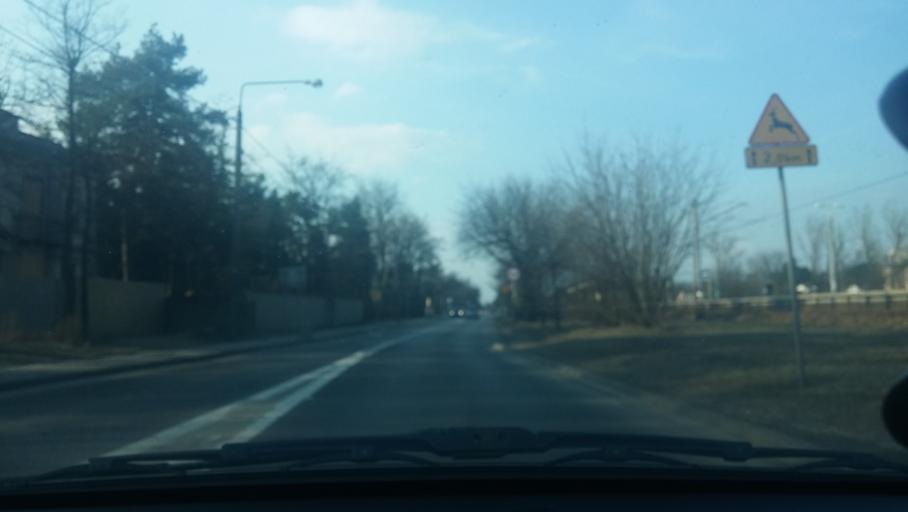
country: PL
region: Masovian Voivodeship
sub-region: Warszawa
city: Wawer
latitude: 52.1847
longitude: 21.1879
